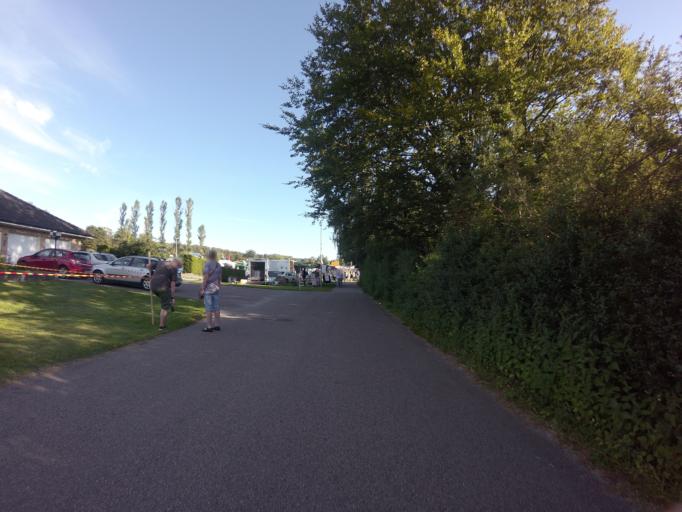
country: SE
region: Skane
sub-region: Sjobo Kommun
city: Sjoebo
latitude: 55.6317
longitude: 13.7111
